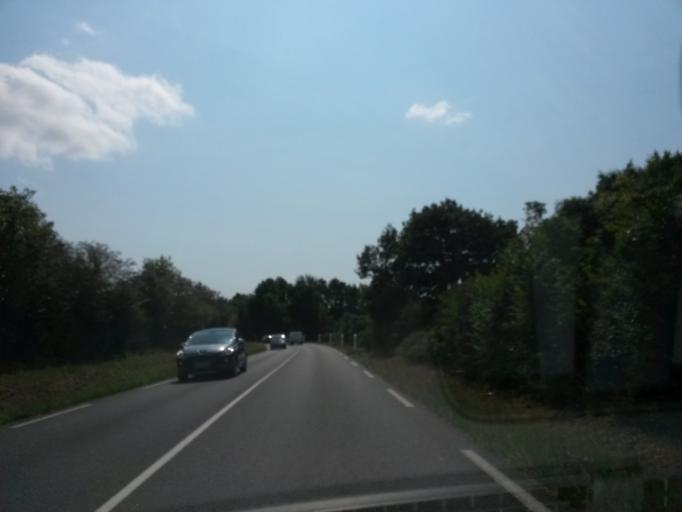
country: FR
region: Pays de la Loire
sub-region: Departement de la Vendee
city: Jard-sur-Mer
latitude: 46.4331
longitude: -1.5780
